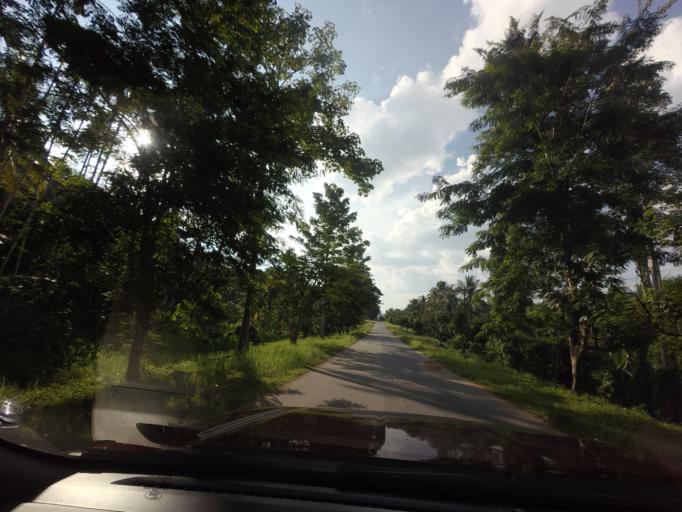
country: TH
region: Yala
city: Ban Nang Sata
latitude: 6.2124
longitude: 101.2332
